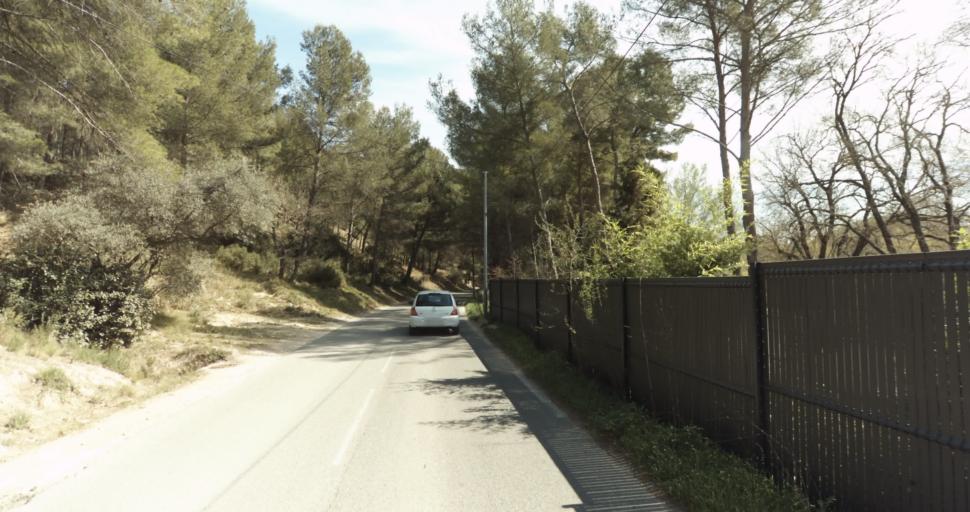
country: FR
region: Provence-Alpes-Cote d'Azur
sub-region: Departement des Bouches-du-Rhone
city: Ventabren
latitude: 43.5267
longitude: 5.2901
